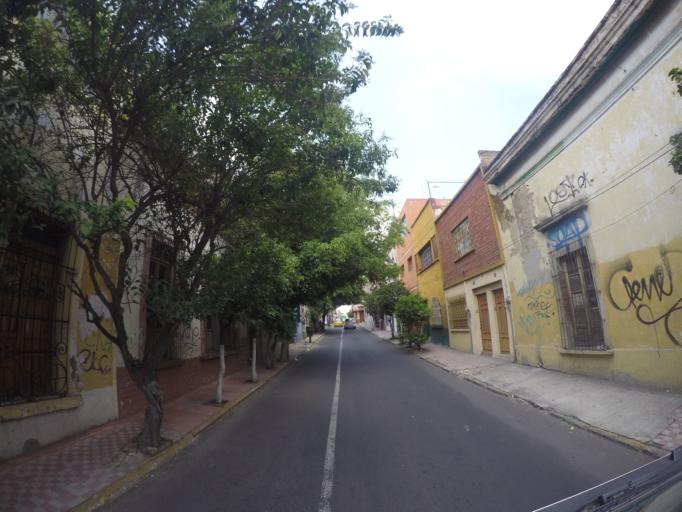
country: MX
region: Jalisco
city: Guadalajara
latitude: 20.6811
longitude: -103.3445
